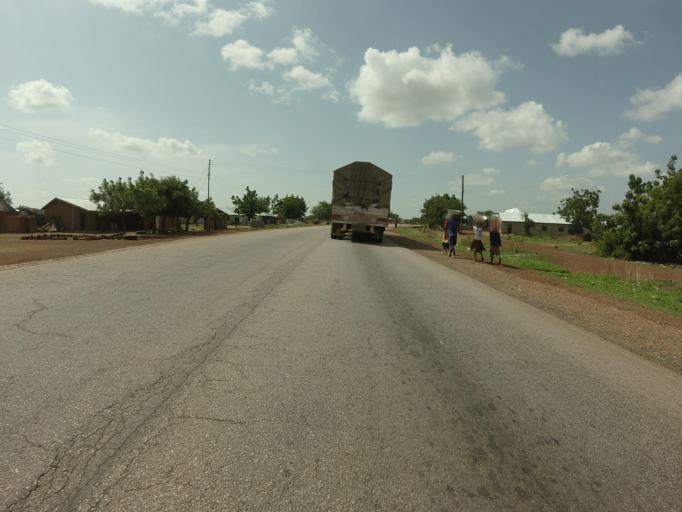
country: GH
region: Northern
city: Savelugu
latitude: 9.8749
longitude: -0.8723
